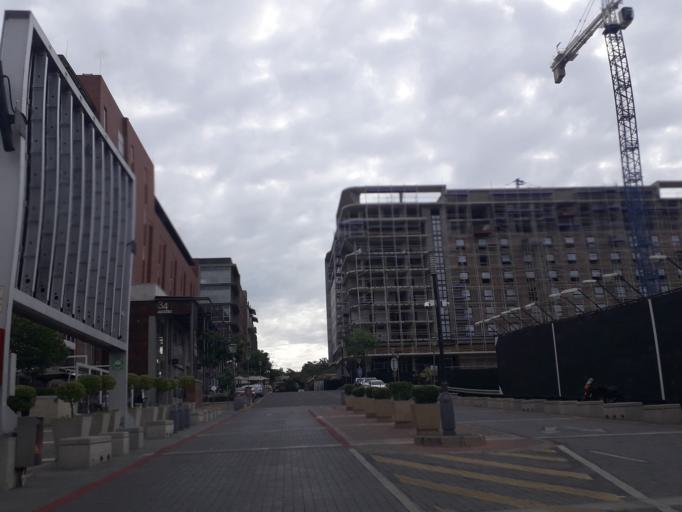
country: ZA
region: Gauteng
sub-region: City of Johannesburg Metropolitan Municipality
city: Johannesburg
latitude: -26.1313
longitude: 28.0687
